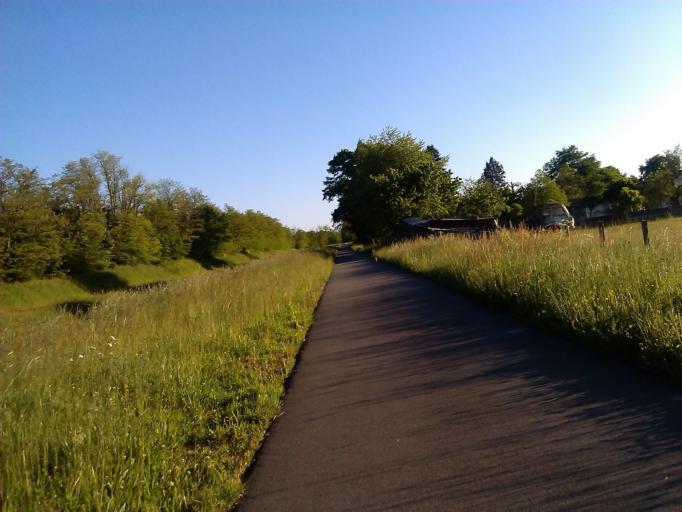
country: FR
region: Auvergne
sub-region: Departement de l'Allier
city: Dompierre-sur-Besbre
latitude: 46.5308
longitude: 3.6970
